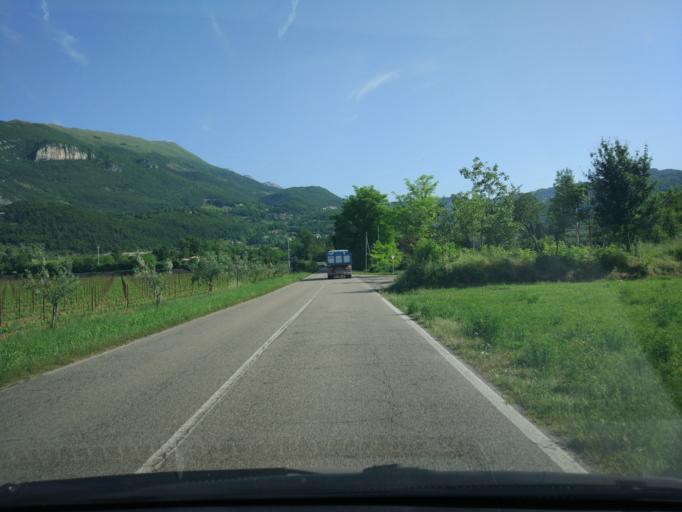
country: IT
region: Veneto
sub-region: Provincia di Verona
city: Caprino Veronese
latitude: 45.6024
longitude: 10.8151
